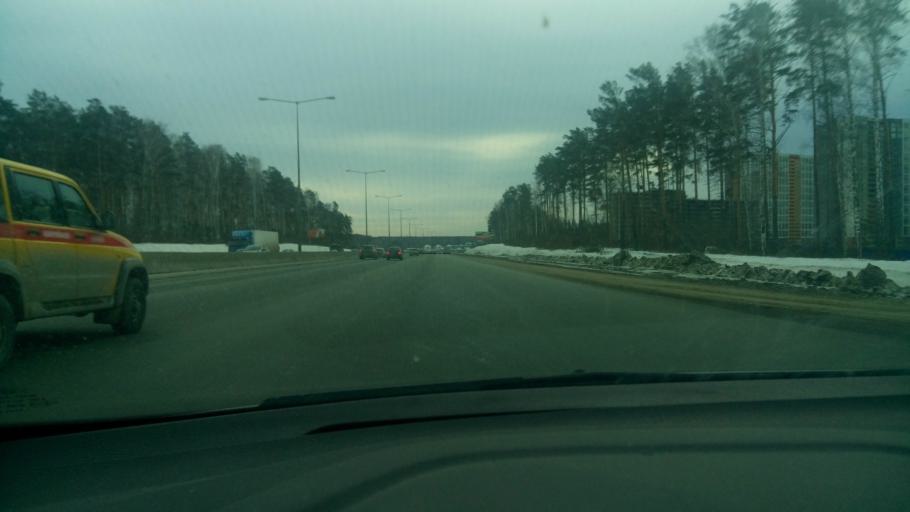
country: RU
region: Sverdlovsk
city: Istok
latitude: 56.7827
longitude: 60.6972
